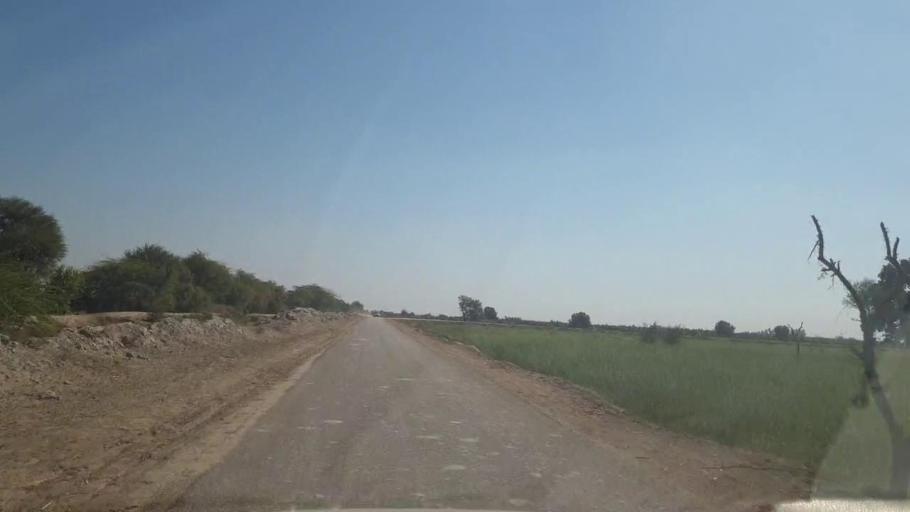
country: PK
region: Sindh
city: Mirpur Khas
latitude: 25.4619
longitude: 69.1805
